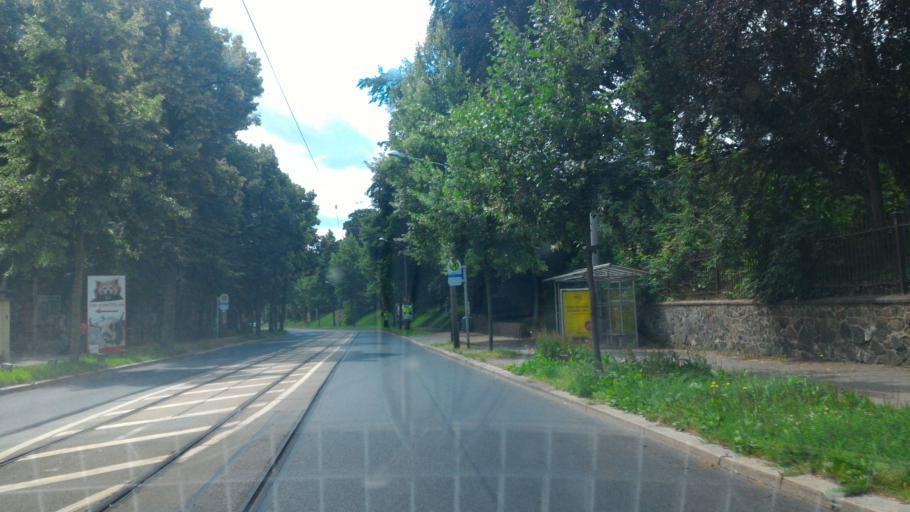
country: DE
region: Saxony
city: Goerlitz
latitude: 51.1424
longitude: 14.9785
